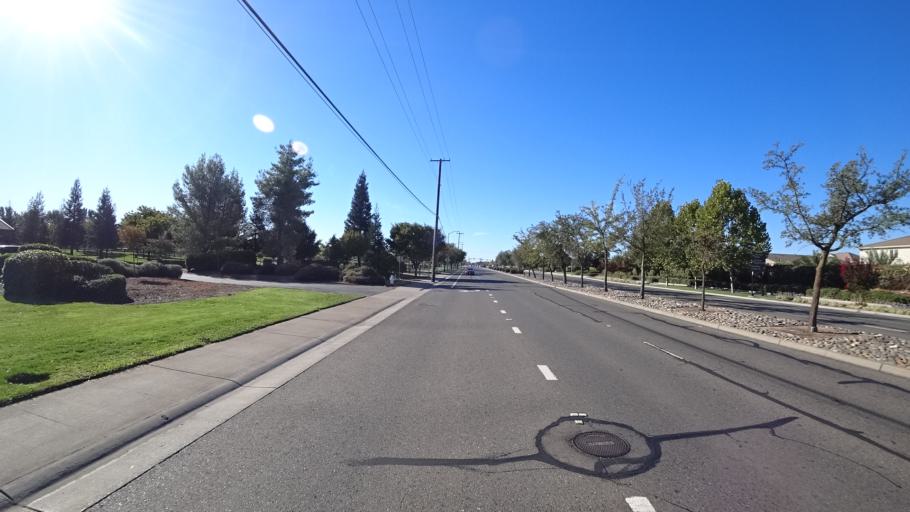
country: US
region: California
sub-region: Sacramento County
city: Elk Grove
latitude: 38.4409
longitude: -121.3715
